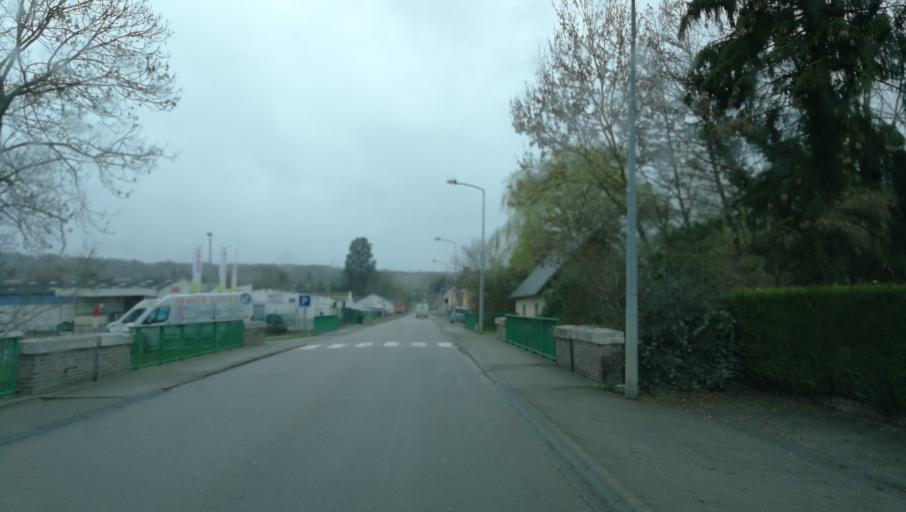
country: FR
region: Haute-Normandie
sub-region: Departement de l'Eure
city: Brionne
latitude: 49.1929
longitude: 0.7188
